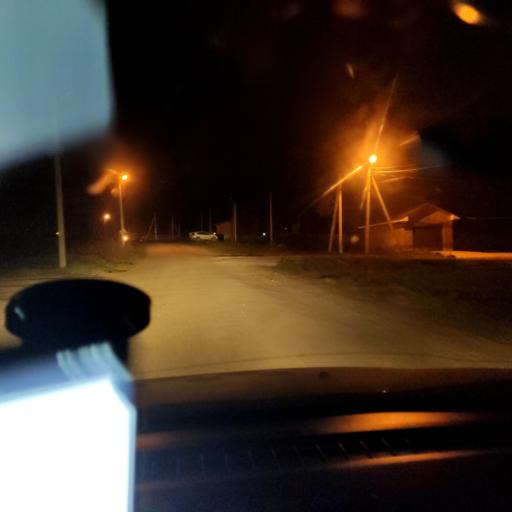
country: RU
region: Bashkortostan
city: Kabakovo
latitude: 54.6031
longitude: 56.1203
